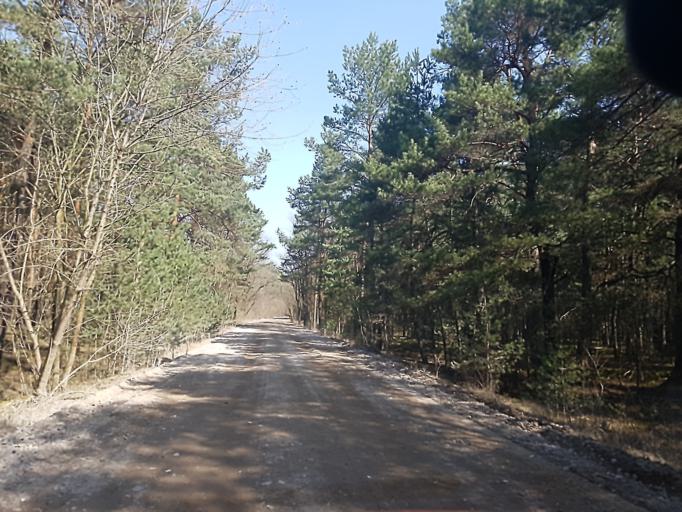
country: DE
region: Brandenburg
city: Tschernitz
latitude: 51.6663
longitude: 14.5665
